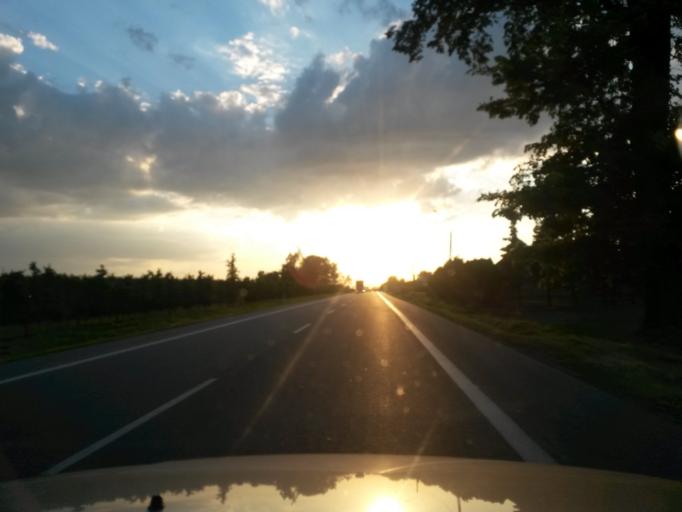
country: PL
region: Lodz Voivodeship
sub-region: Powiat wielunski
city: Czarnozyly
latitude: 51.2515
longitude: 18.5091
